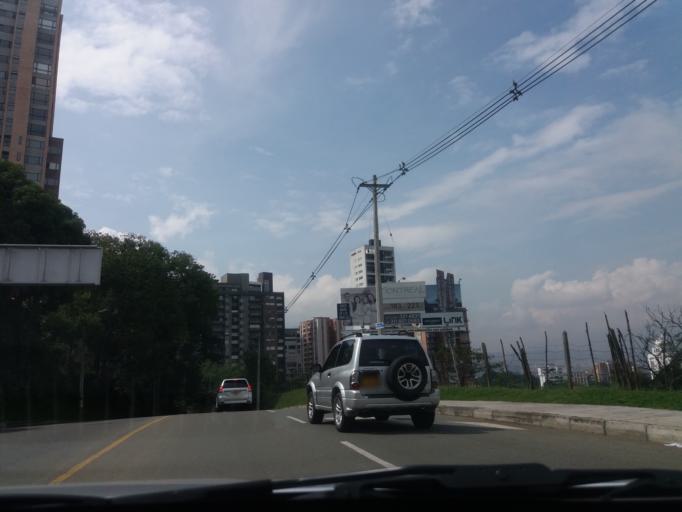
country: CO
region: Antioquia
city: Envigado
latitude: 6.1940
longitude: -75.5727
